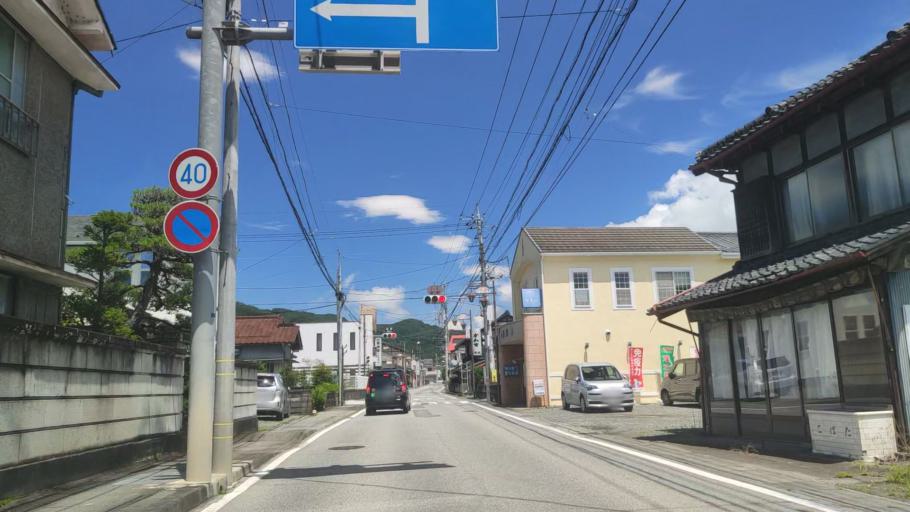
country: JP
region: Yamanashi
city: Ryuo
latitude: 35.4933
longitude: 138.4609
